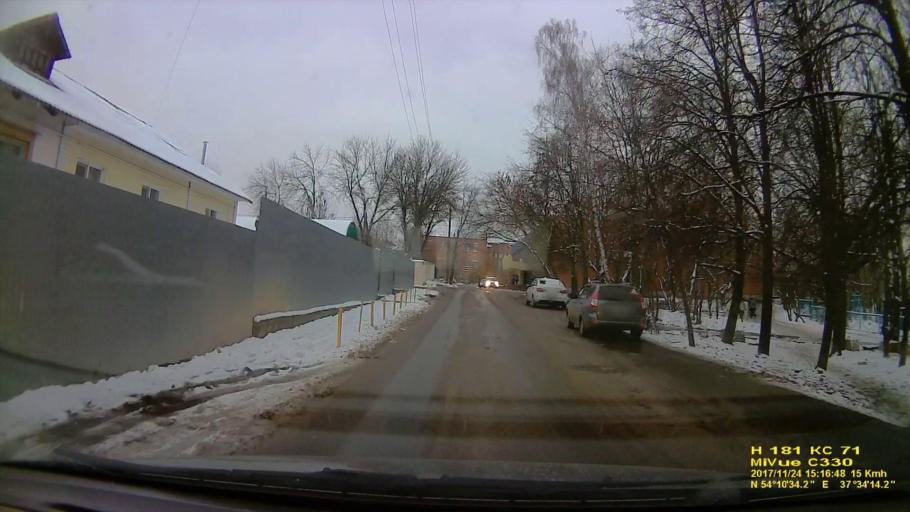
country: RU
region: Tula
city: Mendeleyevskiy
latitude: 54.1761
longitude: 37.5706
